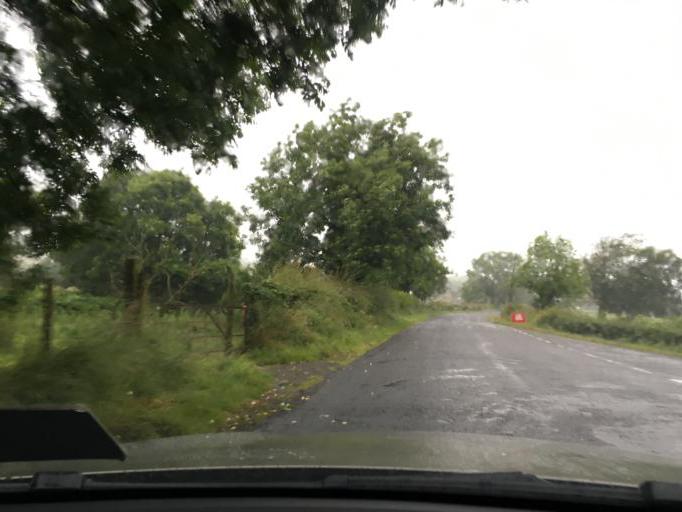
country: GB
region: Northern Ireland
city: Irvinestown
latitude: 54.5550
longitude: -7.8275
